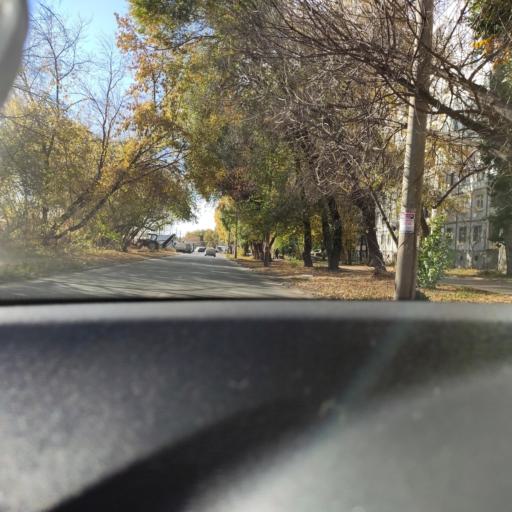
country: RU
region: Samara
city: Samara
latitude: 53.2454
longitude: 50.2556
